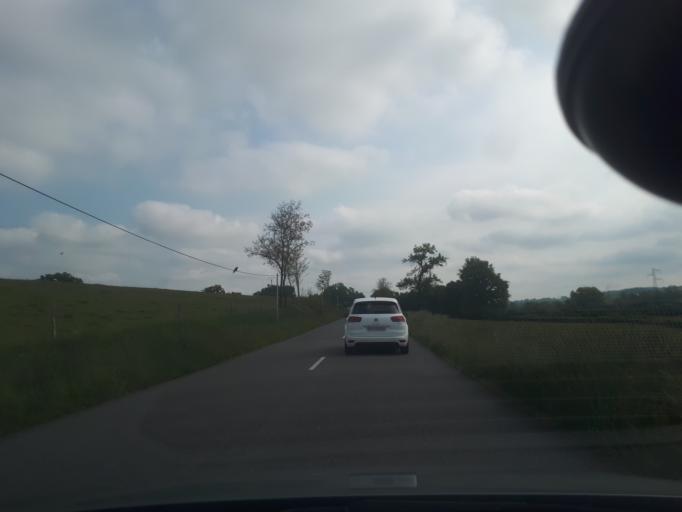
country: FR
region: Auvergne
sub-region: Departement de l'Allier
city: Lapalisse
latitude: 46.3888
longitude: 3.5888
